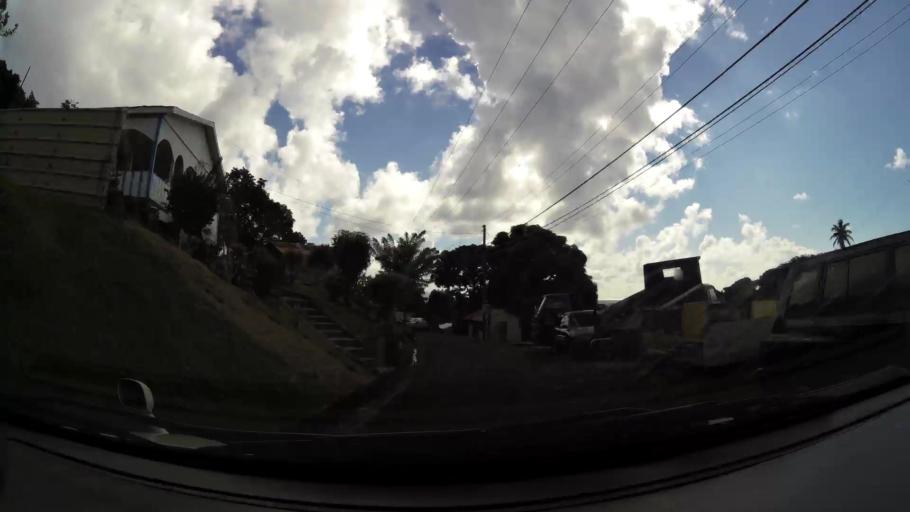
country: VC
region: Saint George
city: Kingstown
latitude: 13.1337
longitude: -61.1926
